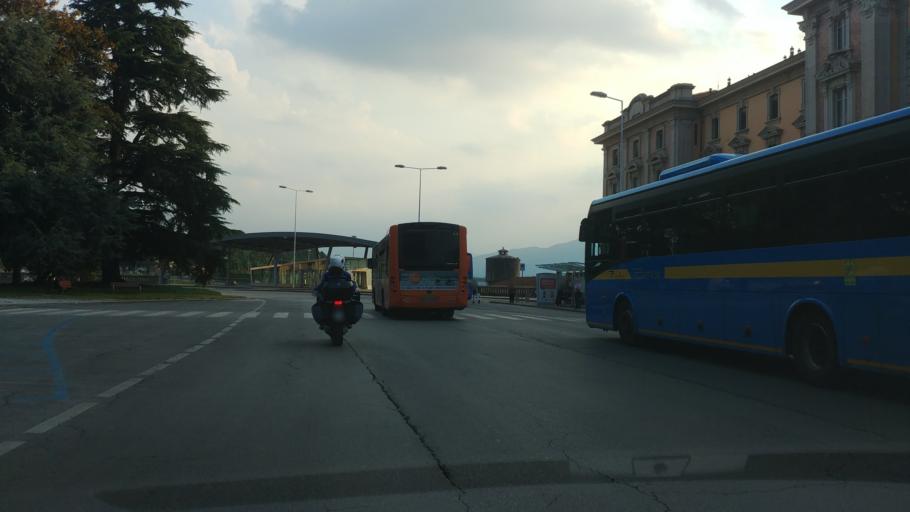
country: IT
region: Piedmont
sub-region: Provincia di Cuneo
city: Cuneo
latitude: 44.3878
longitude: 7.5370
